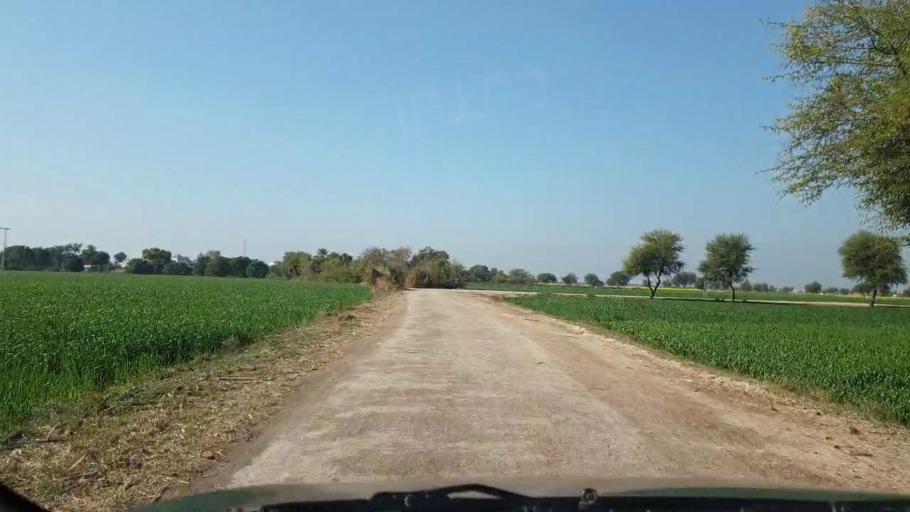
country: PK
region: Sindh
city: Sinjhoro
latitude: 25.9413
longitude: 68.7634
